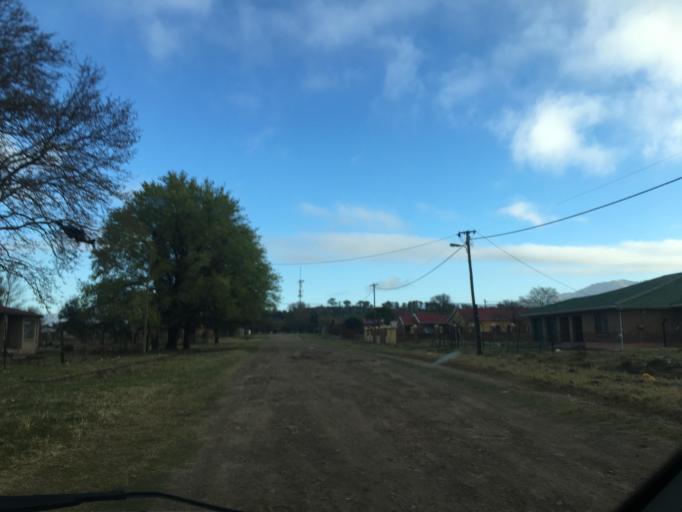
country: ZA
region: Eastern Cape
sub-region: Chris Hani District Municipality
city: Elliot
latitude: -31.3376
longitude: 27.8518
